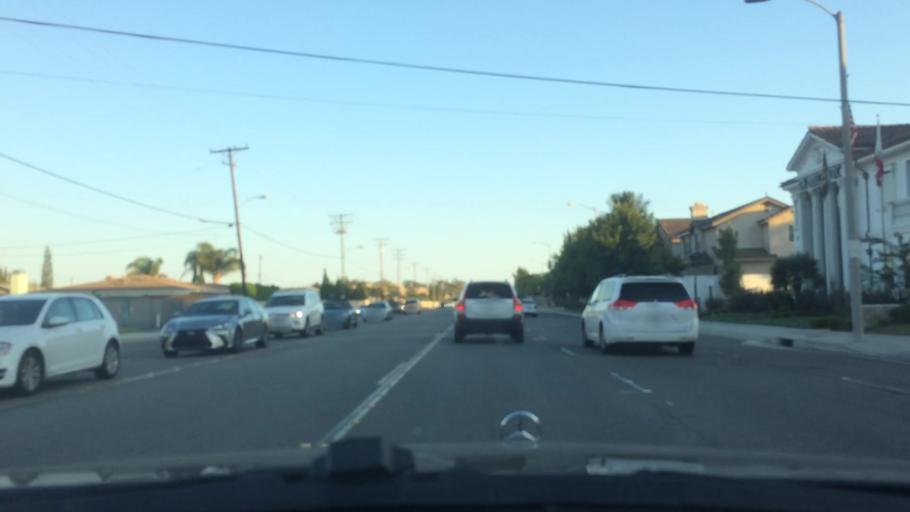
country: US
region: California
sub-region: Orange County
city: Midway City
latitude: 33.7508
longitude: -117.9724
